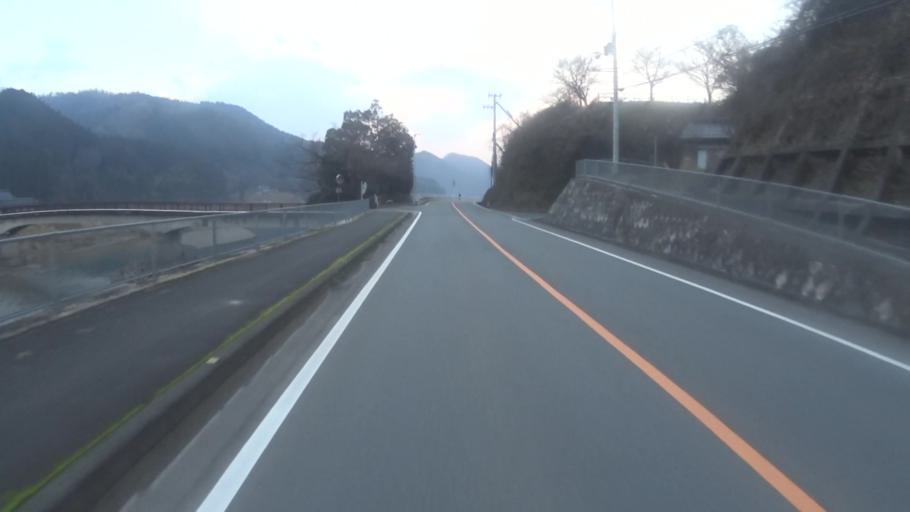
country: JP
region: Kyoto
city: Ayabe
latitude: 35.3346
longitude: 135.3450
